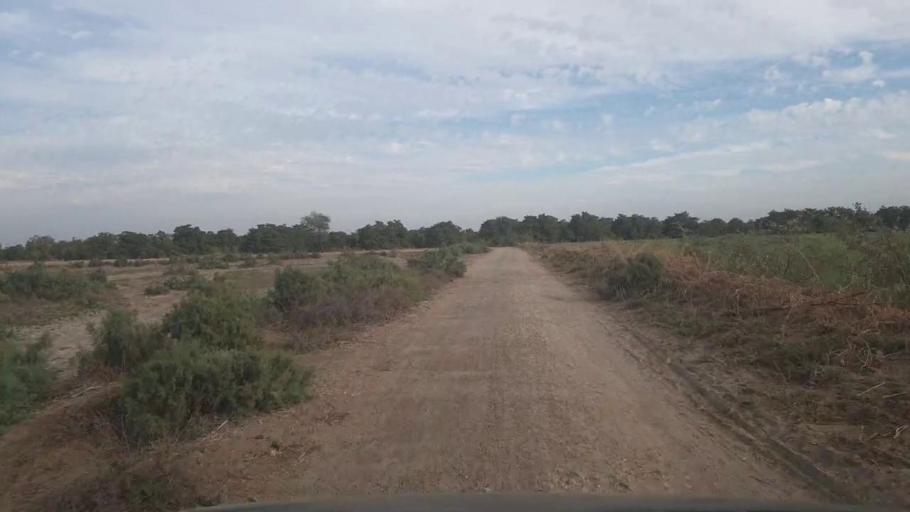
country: PK
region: Sindh
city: Samaro
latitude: 25.3277
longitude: 69.2656
